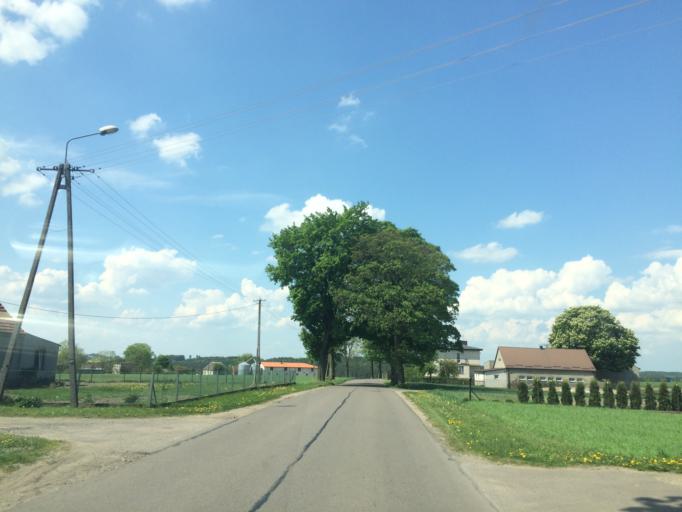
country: PL
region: Warmian-Masurian Voivodeship
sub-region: Powiat ilawski
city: Lubawa
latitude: 53.4355
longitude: 19.7089
